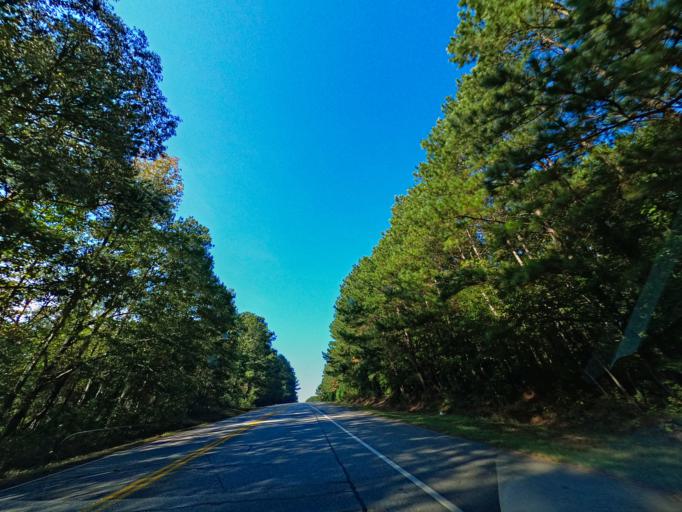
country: US
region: Georgia
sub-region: Coweta County
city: Newnan
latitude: 33.3672
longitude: -84.8886
